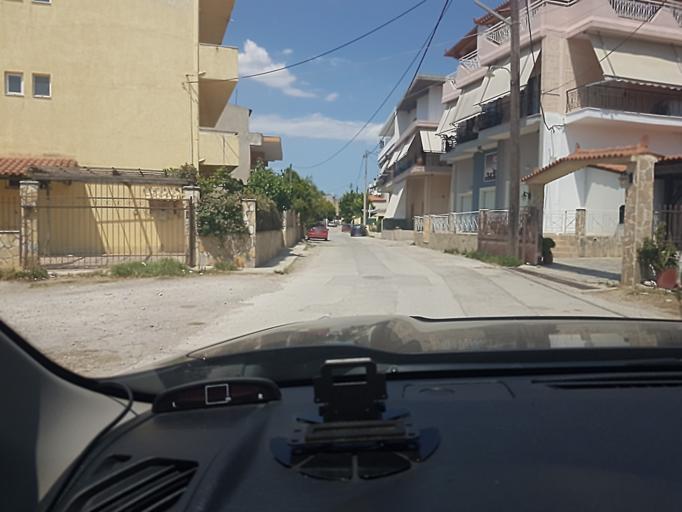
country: GR
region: Central Greece
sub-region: Nomos Evvoias
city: Vasilikon
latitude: 38.4247
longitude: 23.6643
